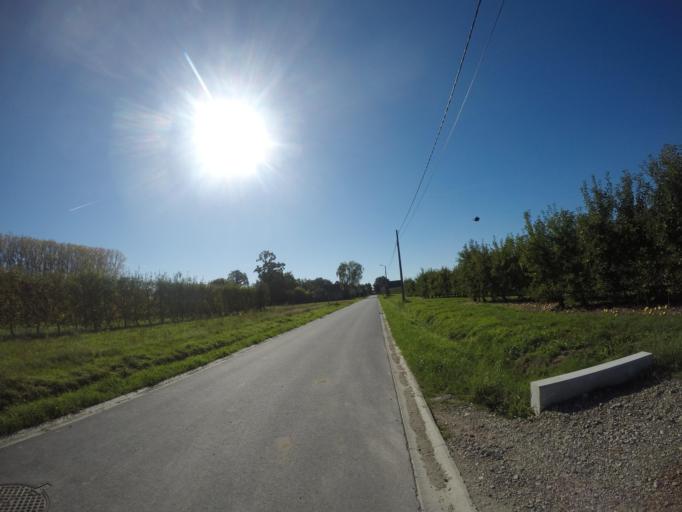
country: BE
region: Flanders
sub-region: Provincie Limburg
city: Alken
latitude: 50.8826
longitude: 5.3221
